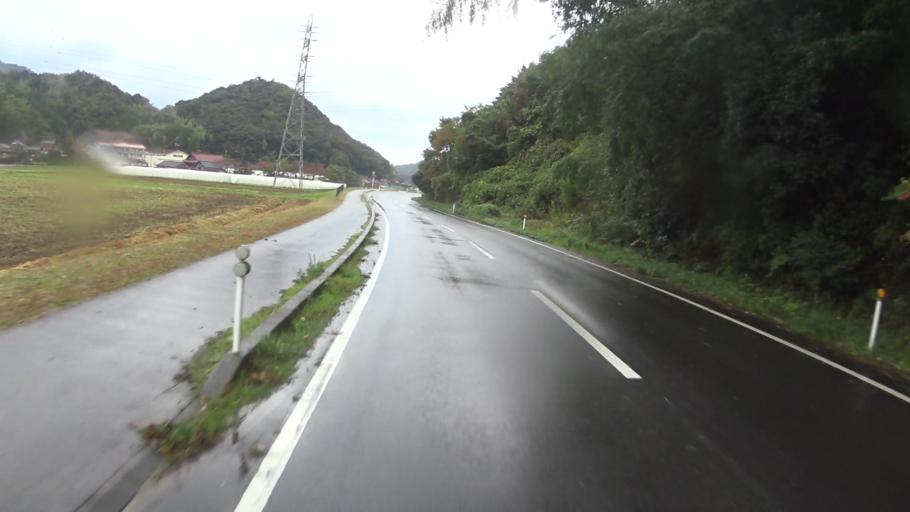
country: JP
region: Kyoto
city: Miyazu
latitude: 35.5049
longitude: 135.1805
